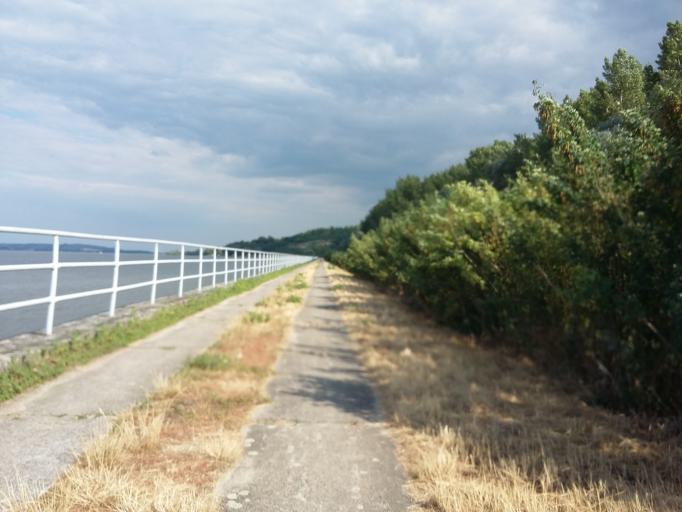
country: CZ
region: South Moravian
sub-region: Okres Breclav
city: Dolni Dunajovice
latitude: 48.8926
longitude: 16.6451
